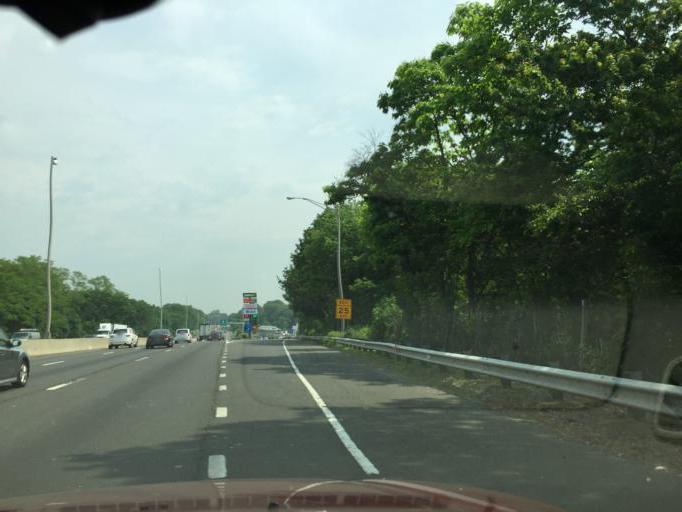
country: US
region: Connecticut
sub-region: Fairfield County
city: Darien
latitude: 41.0779
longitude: -73.4640
